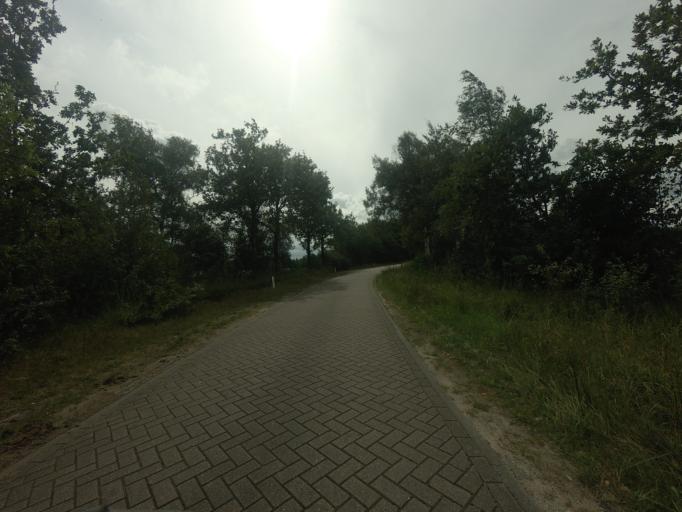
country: NL
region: Drenthe
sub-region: Gemeente Westerveld
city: Dwingeloo
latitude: 52.9936
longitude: 6.3794
